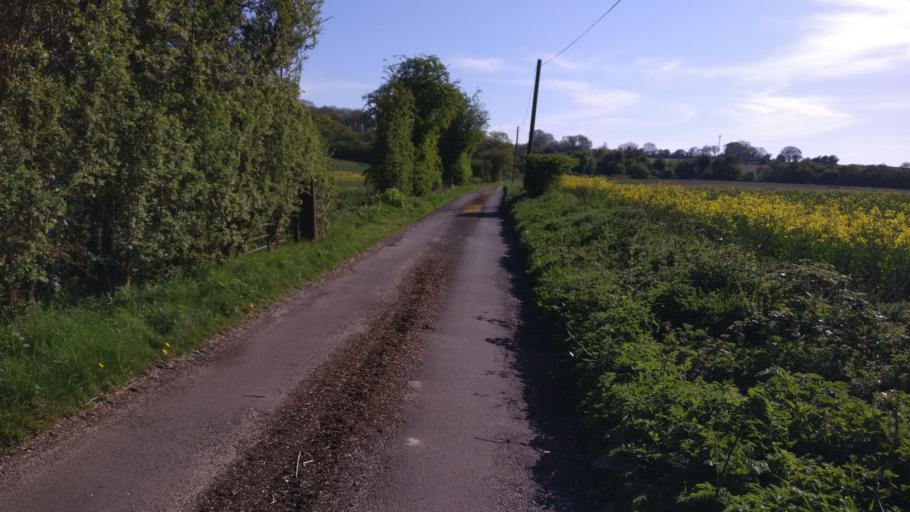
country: GB
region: England
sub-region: Hampshire
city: Basingstoke
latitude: 51.2320
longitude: -1.0719
